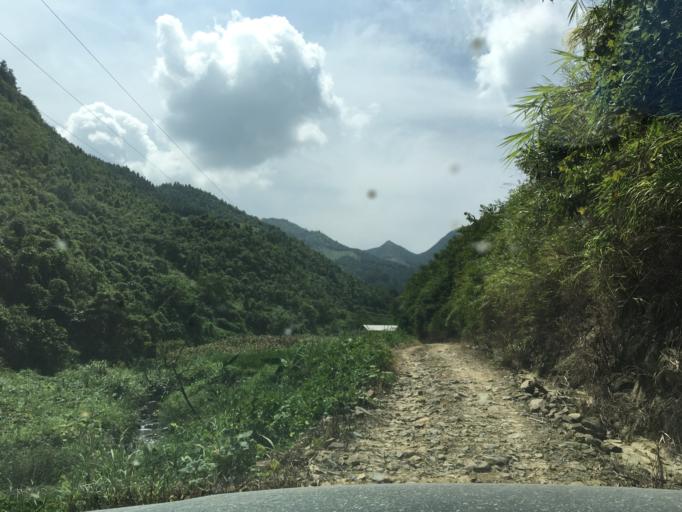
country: CN
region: Guangxi Zhuangzu Zizhiqu
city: Xinzhou
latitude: 24.9535
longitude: 105.7950
